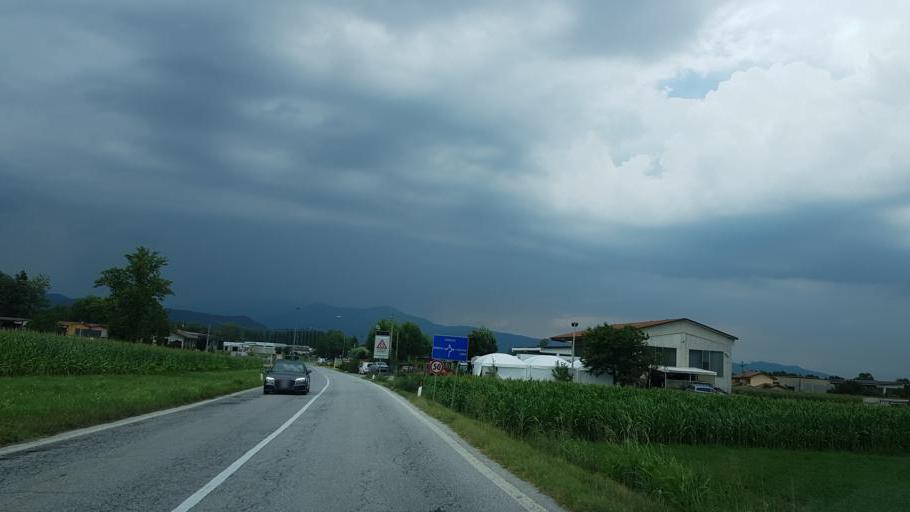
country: IT
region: Piedmont
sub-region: Provincia di Cuneo
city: Cervasca
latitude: 44.3890
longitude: 7.4606
